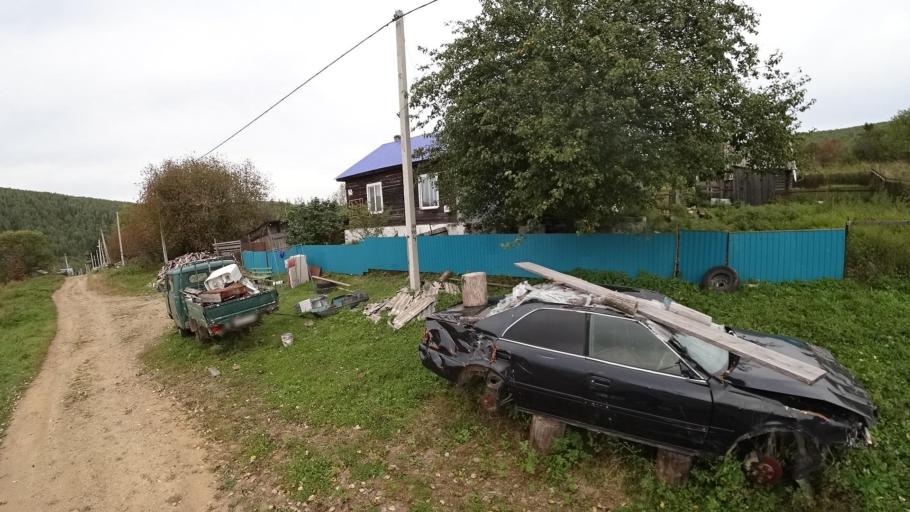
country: RU
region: Jewish Autonomous Oblast
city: Khingansk
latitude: 49.1281
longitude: 131.2030
